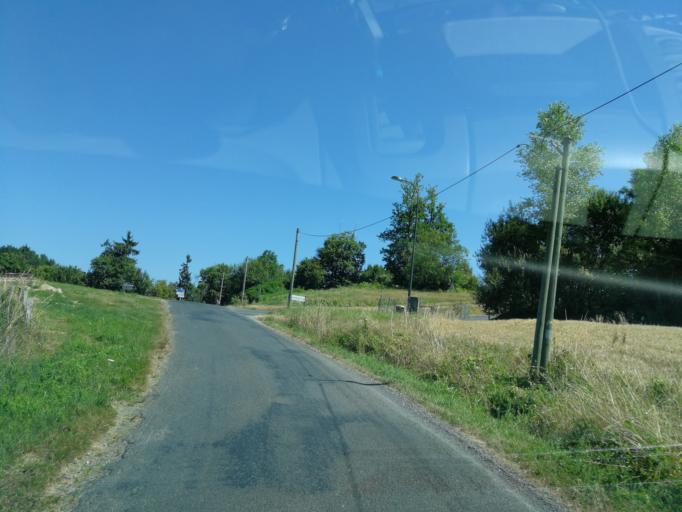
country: FR
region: Limousin
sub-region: Departement de la Correze
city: Sainte-Fereole
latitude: 45.2320
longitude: 1.5953
